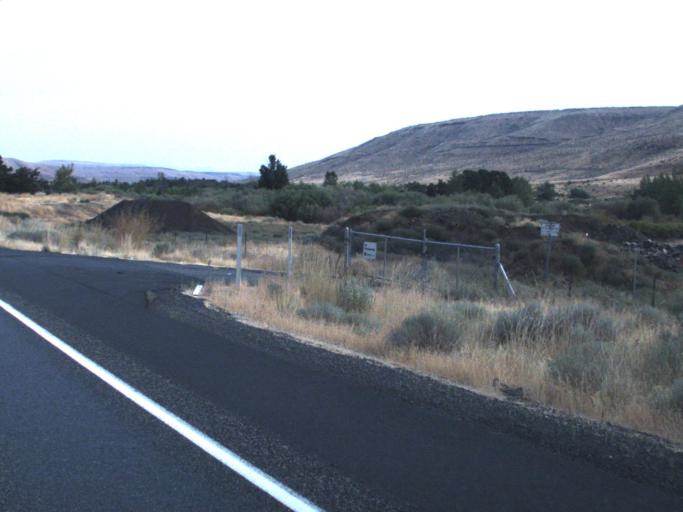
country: US
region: Washington
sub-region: Yakima County
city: Toppenish
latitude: 46.1663
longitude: -120.5058
